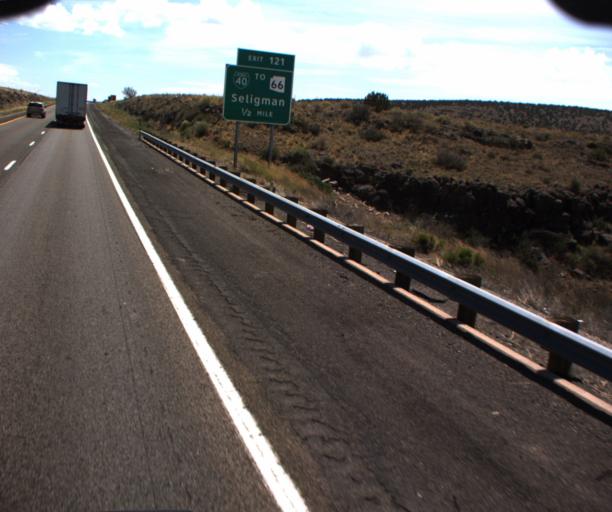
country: US
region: Arizona
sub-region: Mohave County
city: Peach Springs
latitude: 35.3219
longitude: -112.9064
